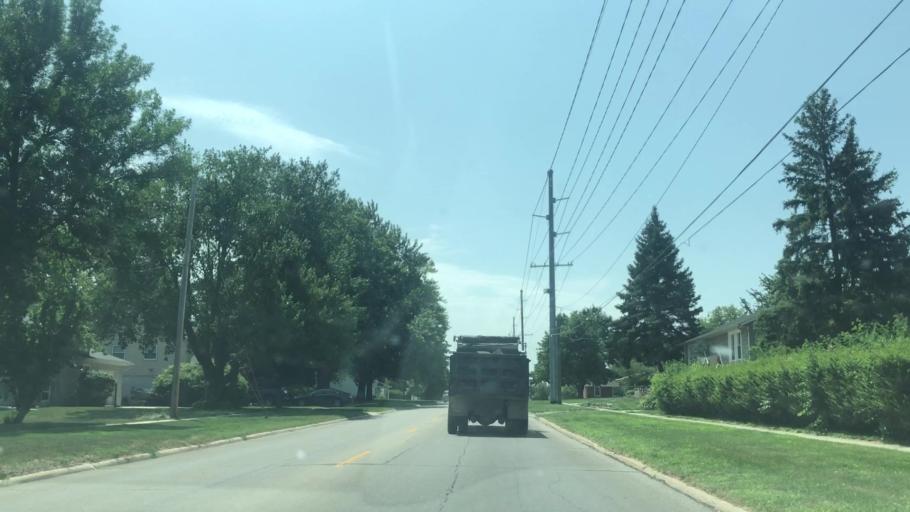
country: US
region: Iowa
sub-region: Marshall County
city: Marshalltown
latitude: 42.0190
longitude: -92.9221
